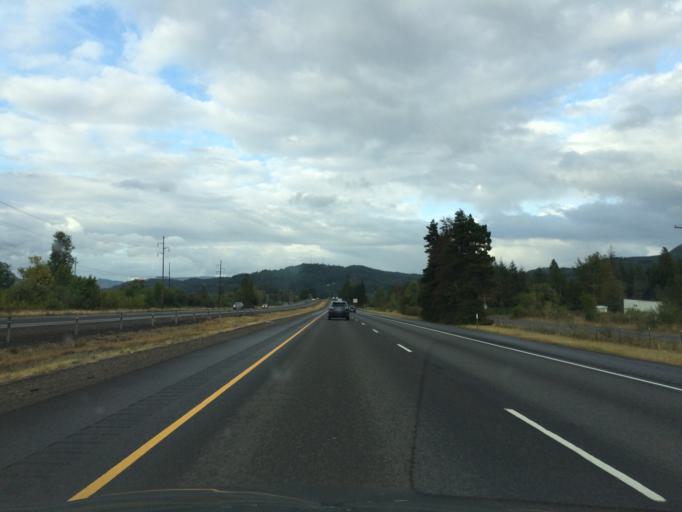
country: US
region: Oregon
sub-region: Lane County
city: Cottage Grove
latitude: 43.7618
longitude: -123.0820
